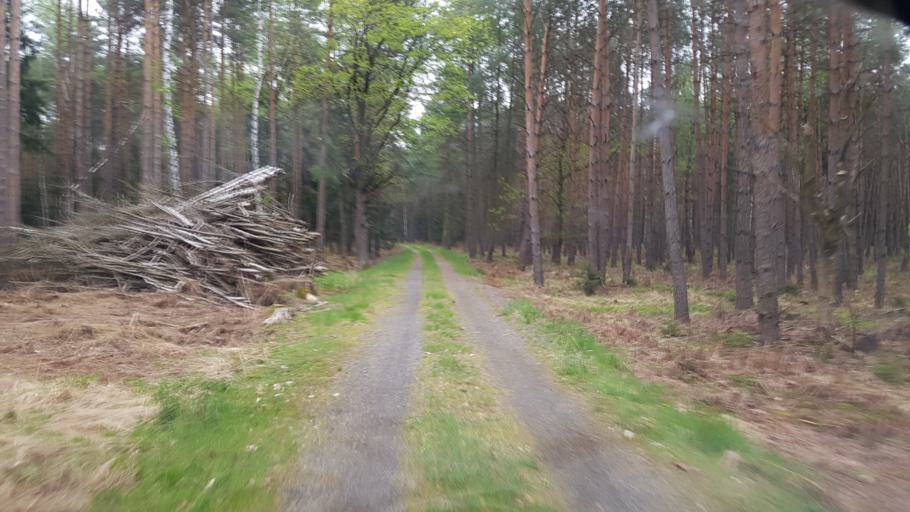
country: DE
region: Brandenburg
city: Schonewalde
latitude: 51.7184
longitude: 13.5402
